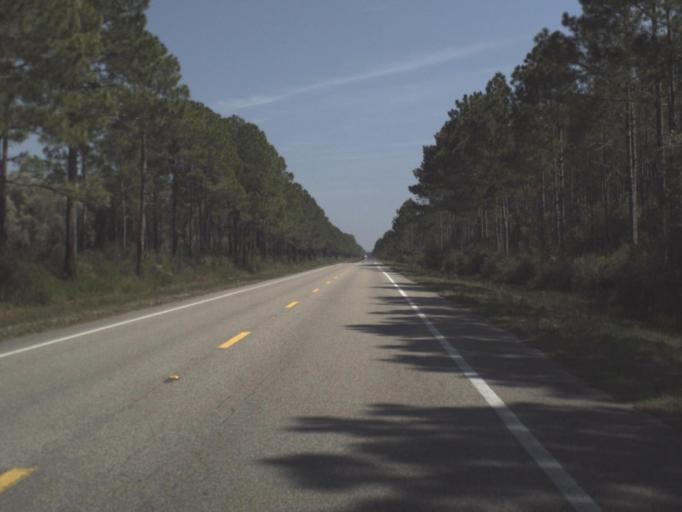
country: US
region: Florida
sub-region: Franklin County
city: Apalachicola
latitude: 29.7327
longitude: -85.1463
